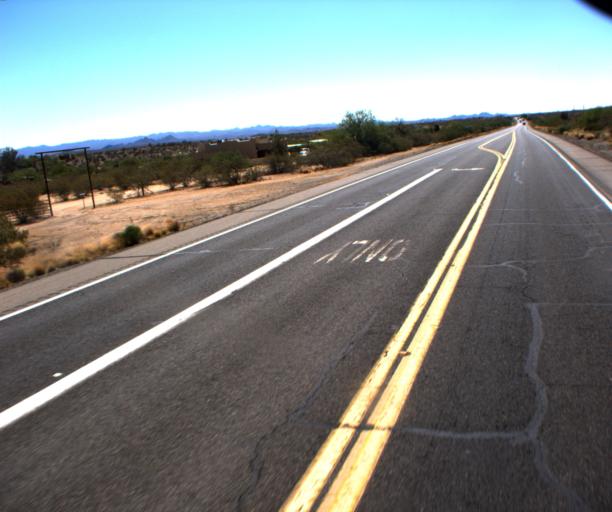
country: US
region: Arizona
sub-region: Maricopa County
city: Wickenburg
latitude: 34.0380
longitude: -112.8280
